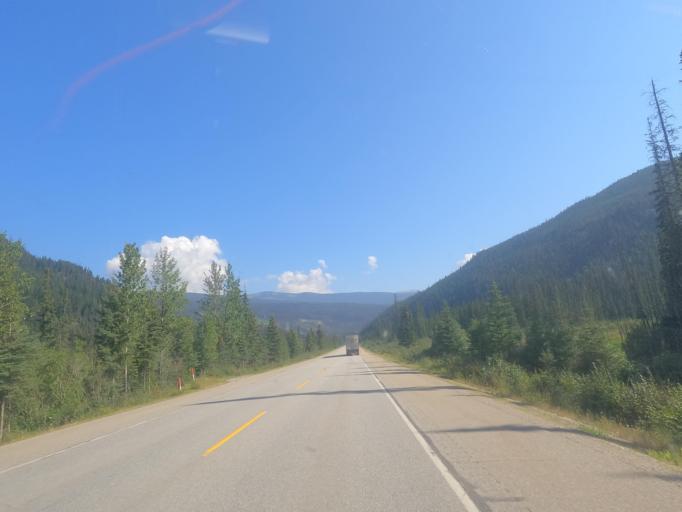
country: CA
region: Alberta
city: Jasper Park Lodge
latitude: 52.8785
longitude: -118.4931
